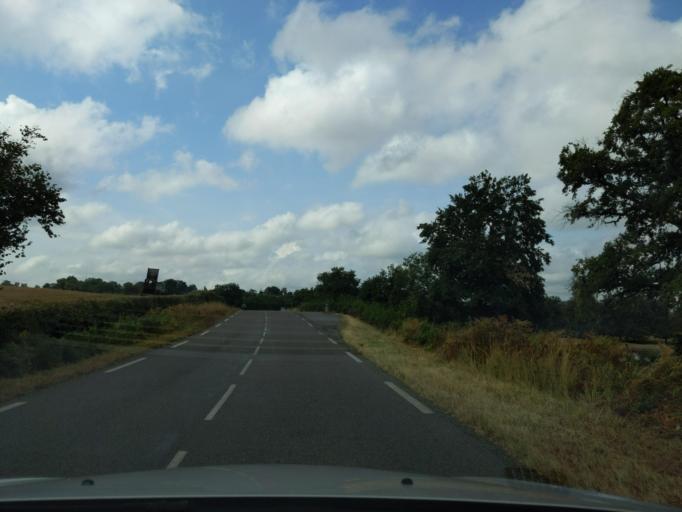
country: FR
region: Bourgogne
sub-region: Departement de la Nievre
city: Luzy
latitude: 46.7308
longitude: 3.9187
